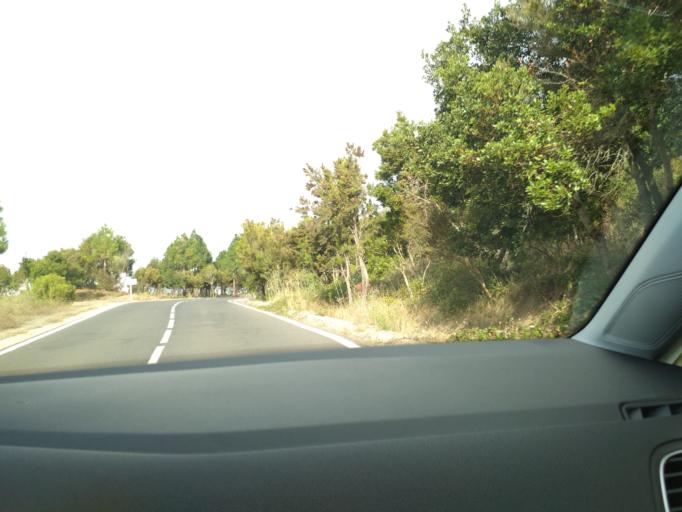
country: ES
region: Canary Islands
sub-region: Provincia de Santa Cruz de Tenerife
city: Garachico
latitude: 28.3295
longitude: -16.7778
